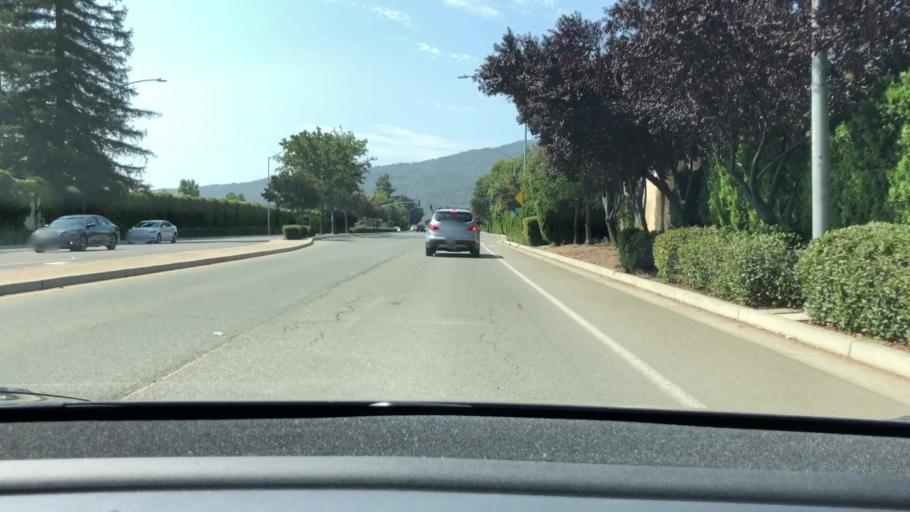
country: US
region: California
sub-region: Santa Clara County
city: Gilroy
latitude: 37.0196
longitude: -121.5991
